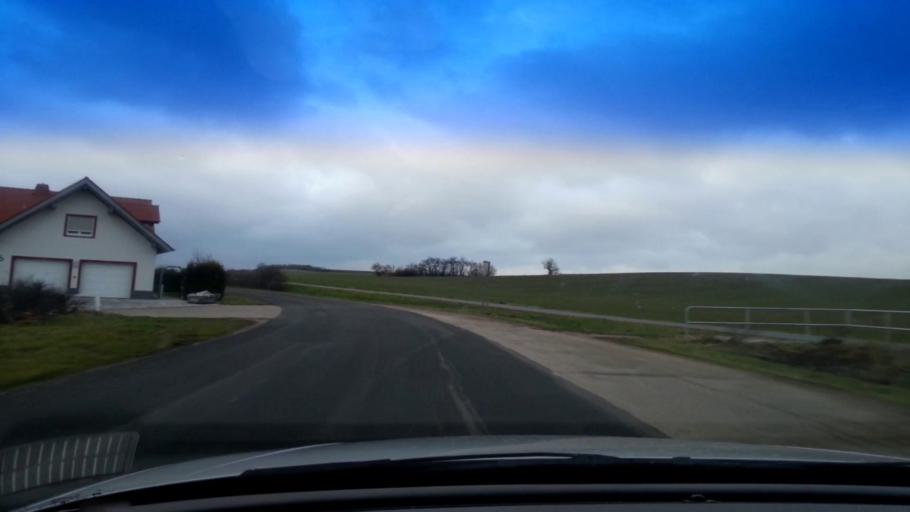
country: DE
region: Bavaria
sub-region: Upper Franconia
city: Walsdorf
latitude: 49.8308
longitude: 10.7806
